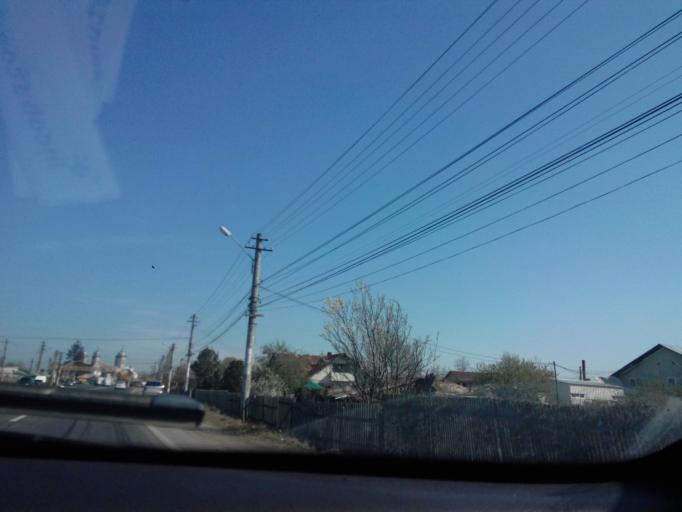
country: RO
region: Prahova
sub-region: Comuna Puchenii Mari
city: Puchenii Mosneni
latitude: 44.8094
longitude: 26.0842
